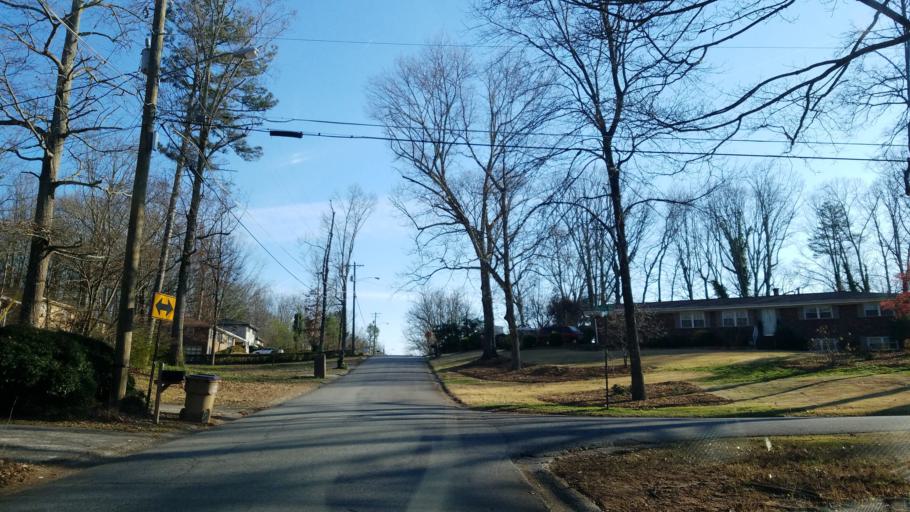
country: US
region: Georgia
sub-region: Cobb County
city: Marietta
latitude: 33.9977
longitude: -84.4957
